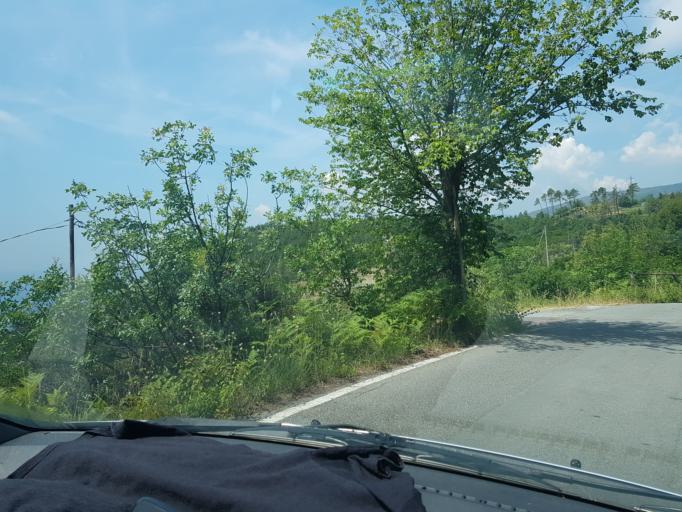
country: IT
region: Liguria
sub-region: Provincia di Genova
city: San Teodoro
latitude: 44.4432
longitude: 8.8437
